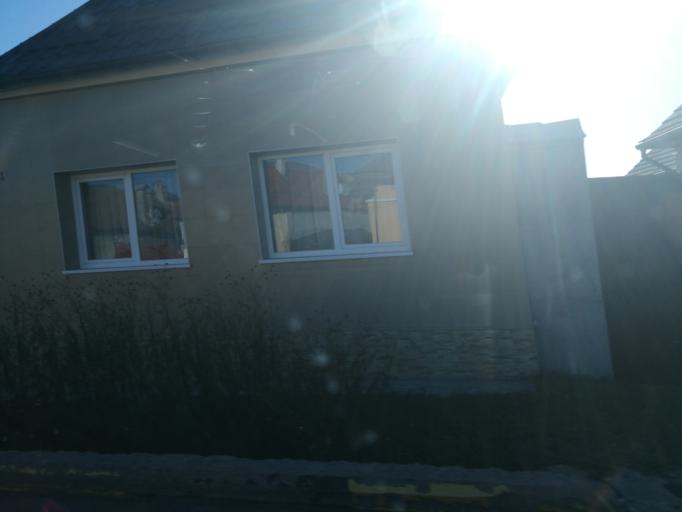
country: RO
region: Brasov
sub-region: Comuna Dumbravita
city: Dumbravita
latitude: 45.7660
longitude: 25.3699
